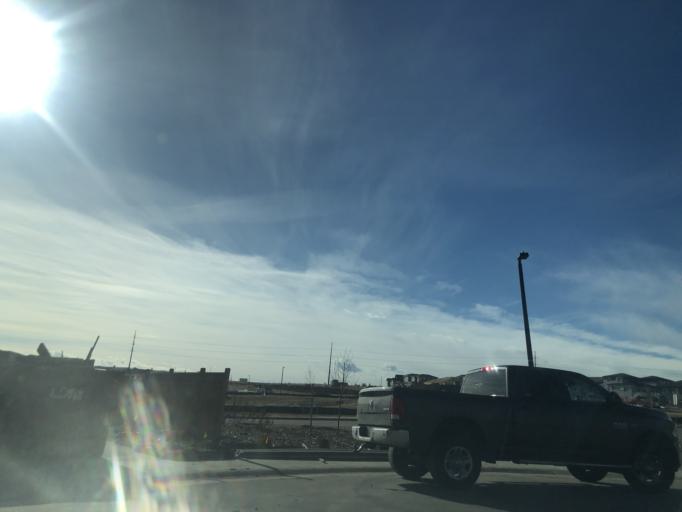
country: US
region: Colorado
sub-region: Douglas County
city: Stonegate
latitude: 39.5553
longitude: -104.8031
